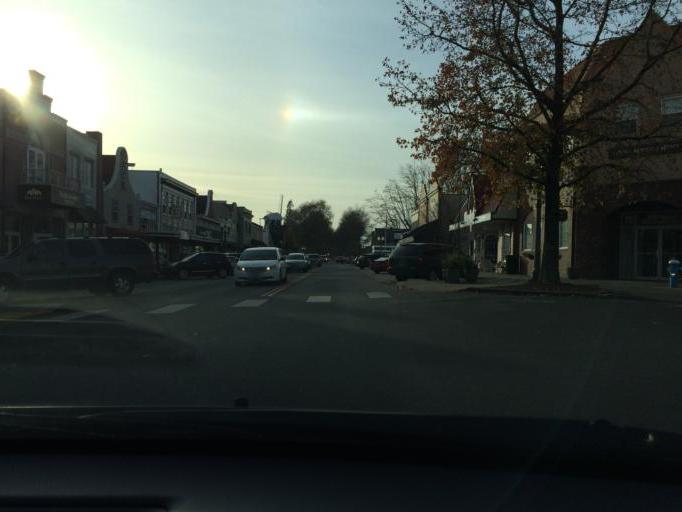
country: US
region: Washington
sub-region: Whatcom County
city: Lynden
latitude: 48.9428
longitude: -122.4529
